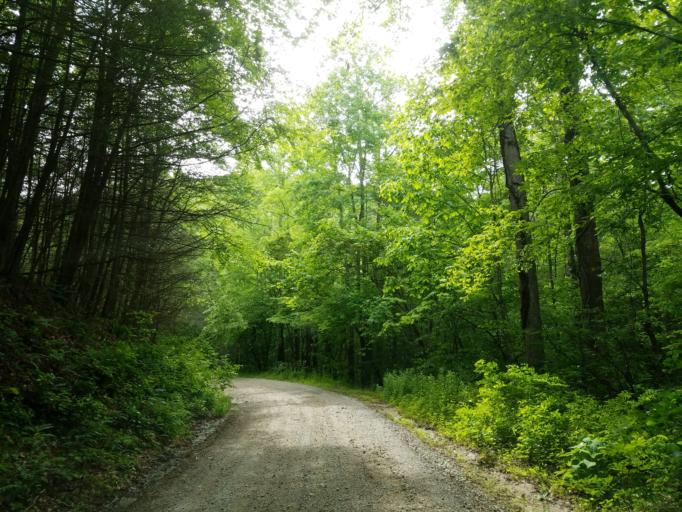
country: US
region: Georgia
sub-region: Union County
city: Blairsville
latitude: 34.7559
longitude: -84.0021
